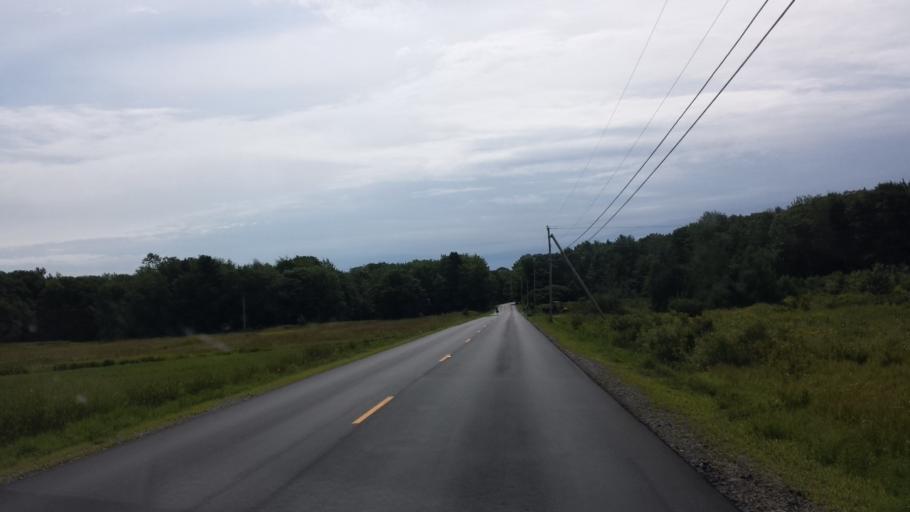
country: US
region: Maine
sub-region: York County
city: Biddeford
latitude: 43.4310
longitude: -70.4030
